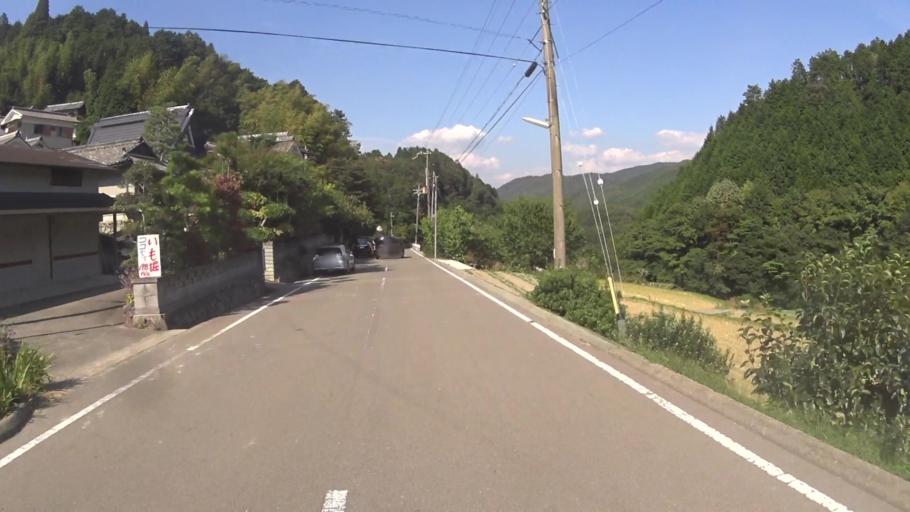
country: JP
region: Kyoto
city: Kameoka
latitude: 34.9182
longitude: 135.5560
